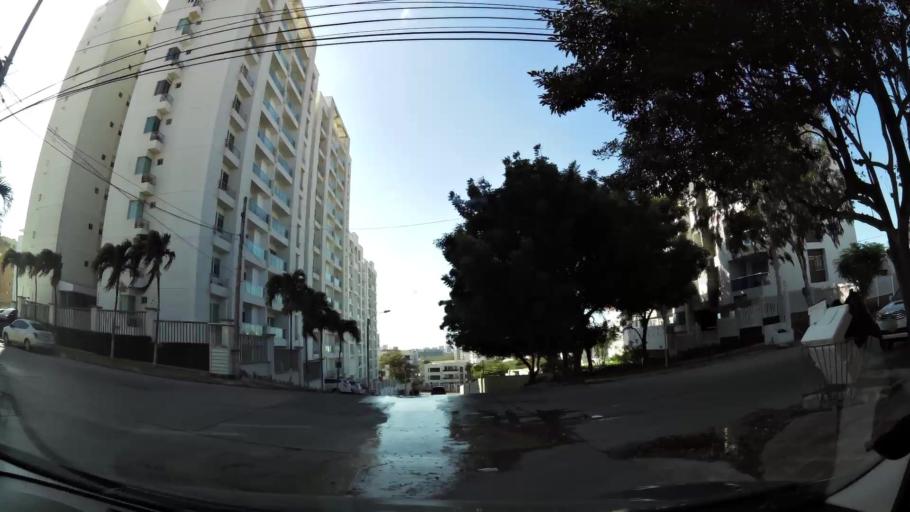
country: CO
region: Atlantico
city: Barranquilla
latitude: 11.0095
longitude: -74.8317
